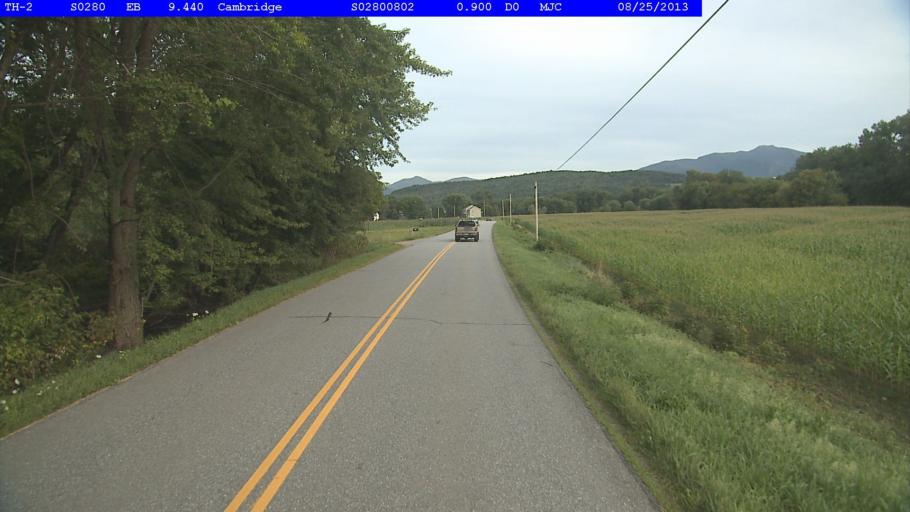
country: US
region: Vermont
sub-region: Chittenden County
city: Jericho
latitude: 44.6512
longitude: -72.8781
